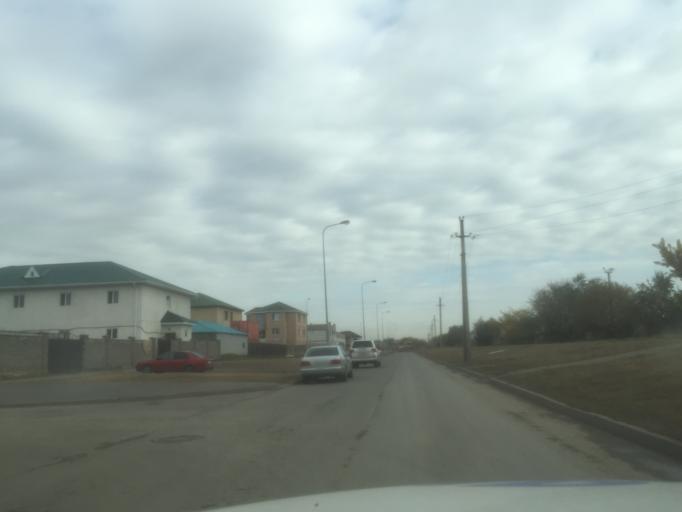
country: KZ
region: Astana Qalasy
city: Astana
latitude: 51.1747
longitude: 71.3756
